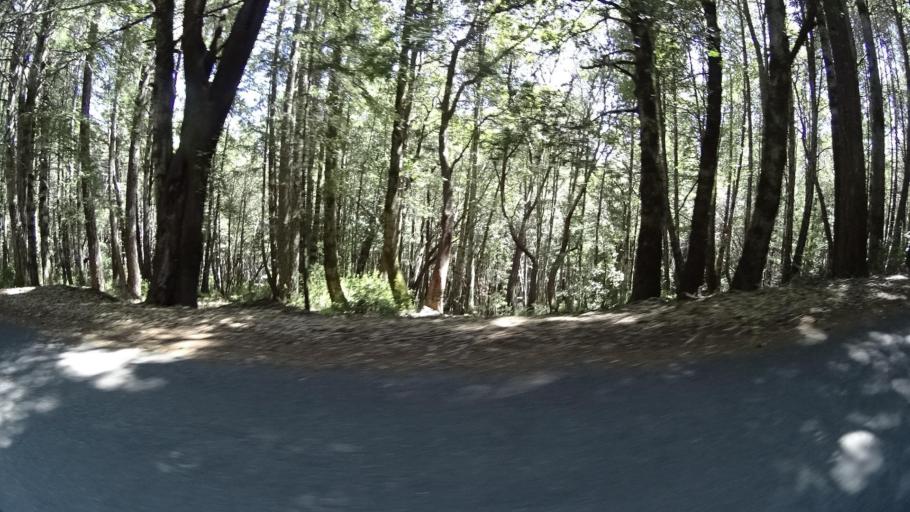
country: US
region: California
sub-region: Humboldt County
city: Redway
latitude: 40.1326
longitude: -123.9782
